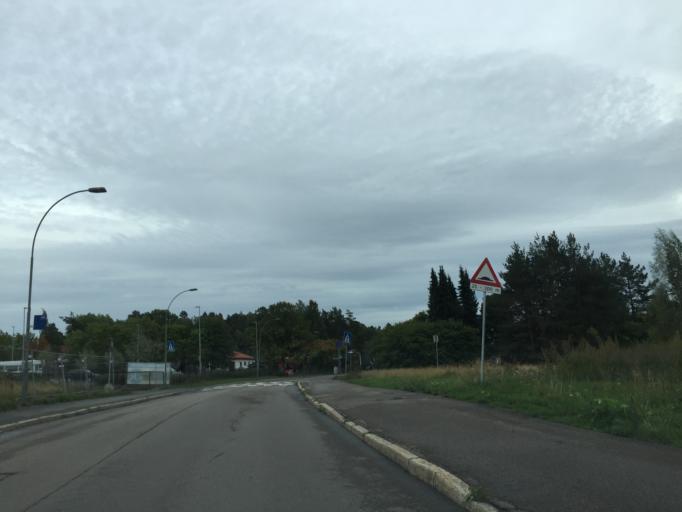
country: NO
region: Oslo
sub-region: Oslo
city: Oslo
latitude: 59.8949
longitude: 10.8203
